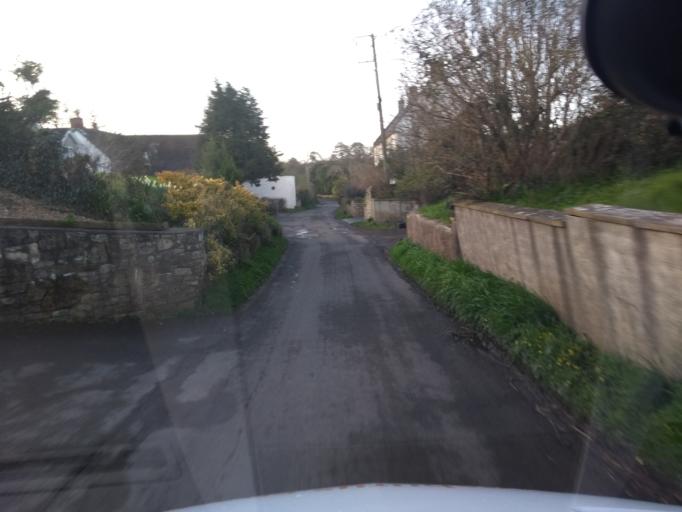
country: GB
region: England
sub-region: Somerset
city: Wedmore
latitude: 51.2263
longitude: -2.8427
